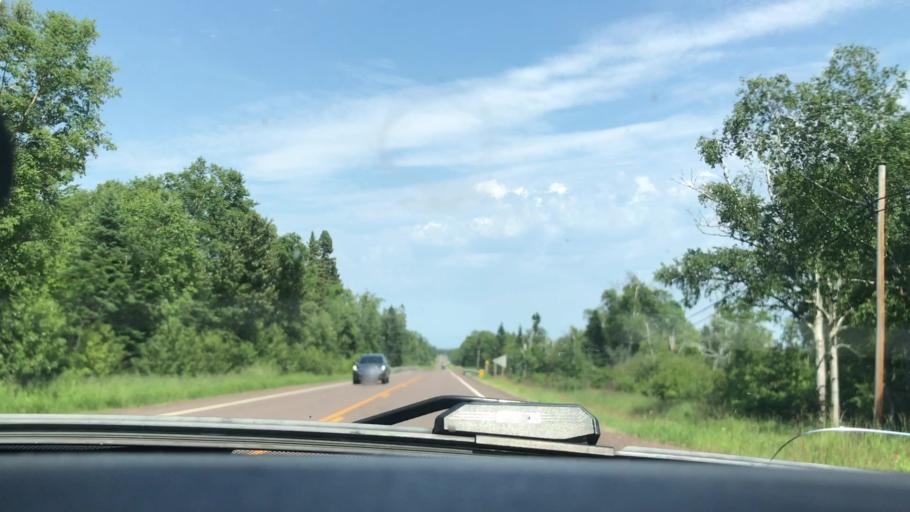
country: US
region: Minnesota
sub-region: Cook County
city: Grand Marais
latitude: 47.6411
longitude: -90.7003
